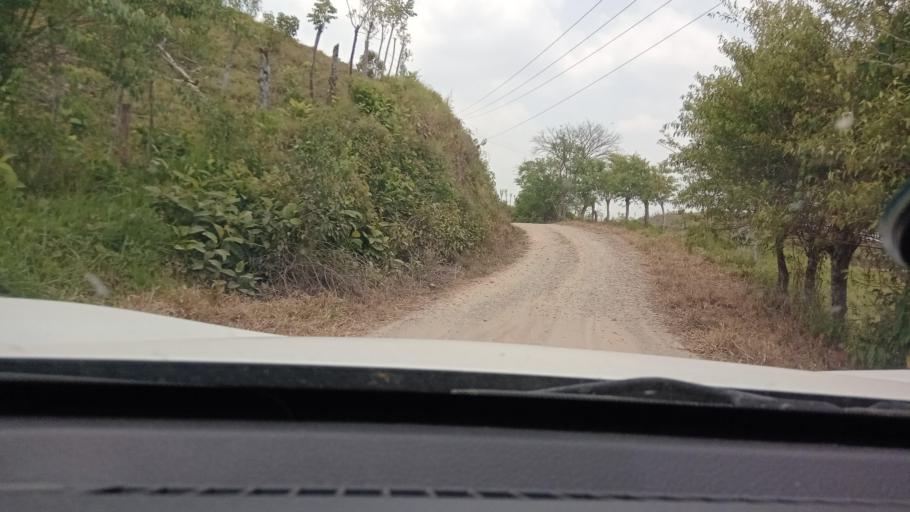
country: MX
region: Tabasco
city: Chontalpa
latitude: 17.5731
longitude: -93.7096
